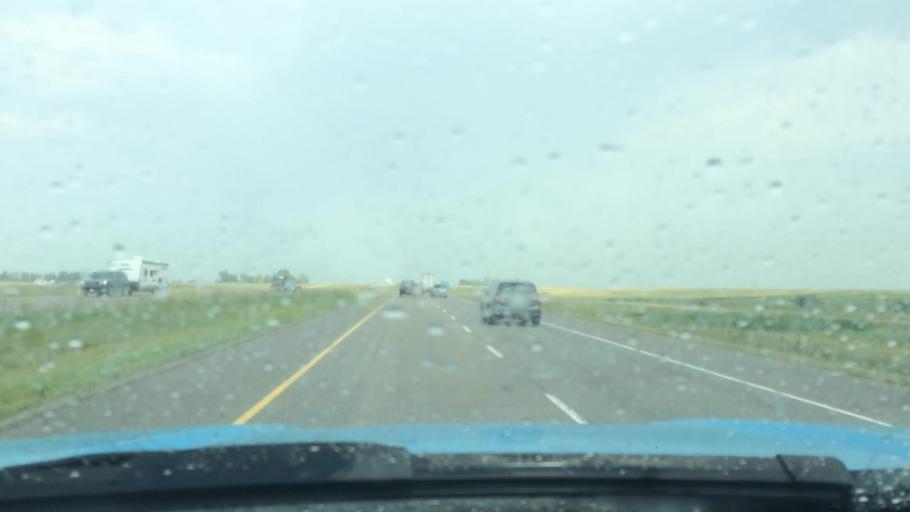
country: CA
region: Alberta
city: Carstairs
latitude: 51.6393
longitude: -114.0254
